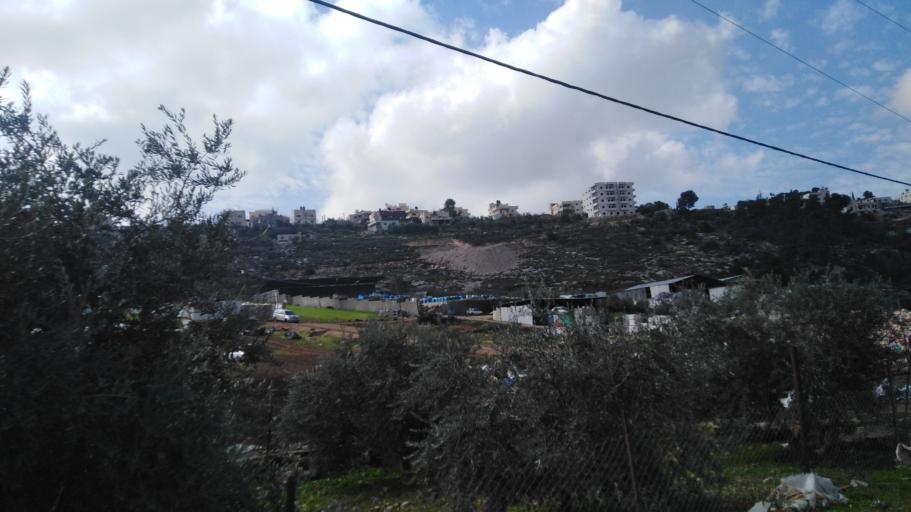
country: PS
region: West Bank
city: Idhna
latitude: 31.5565
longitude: 34.9874
